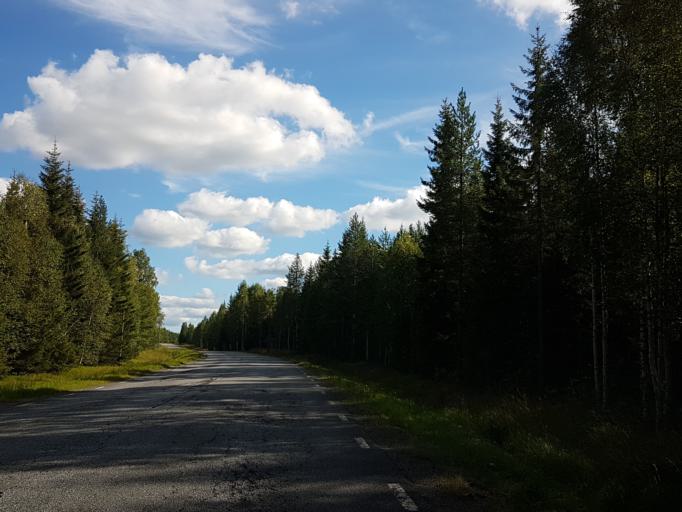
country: SE
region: Vaesterbotten
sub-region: Skelleftea Kommun
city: Burtraesk
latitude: 64.3271
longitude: 20.5265
